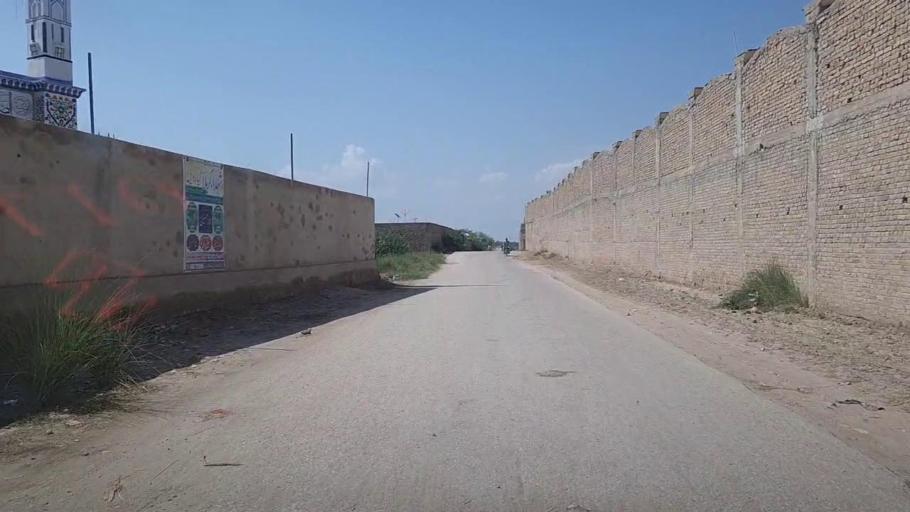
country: PK
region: Sindh
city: Khairpur
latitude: 28.0659
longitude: 69.6442
